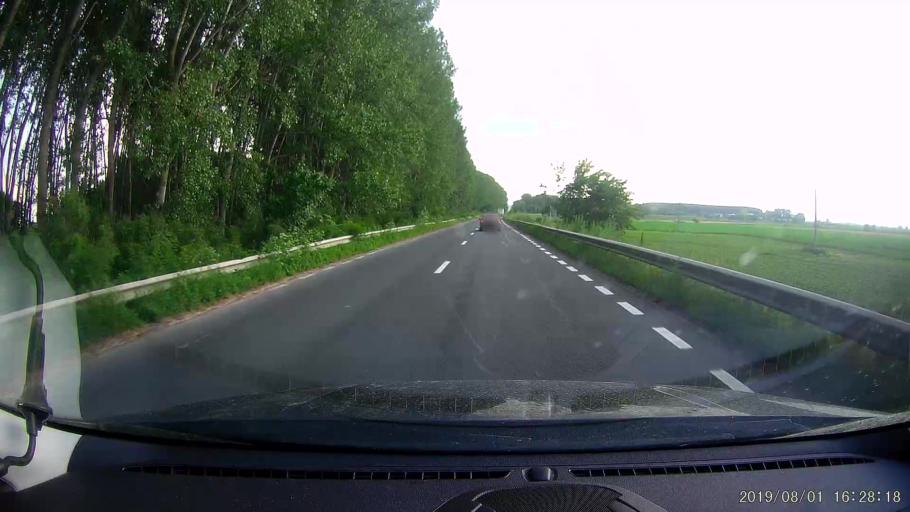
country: BG
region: Silistra
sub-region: Obshtina Silistra
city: Silistra
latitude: 44.1493
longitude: 27.3103
